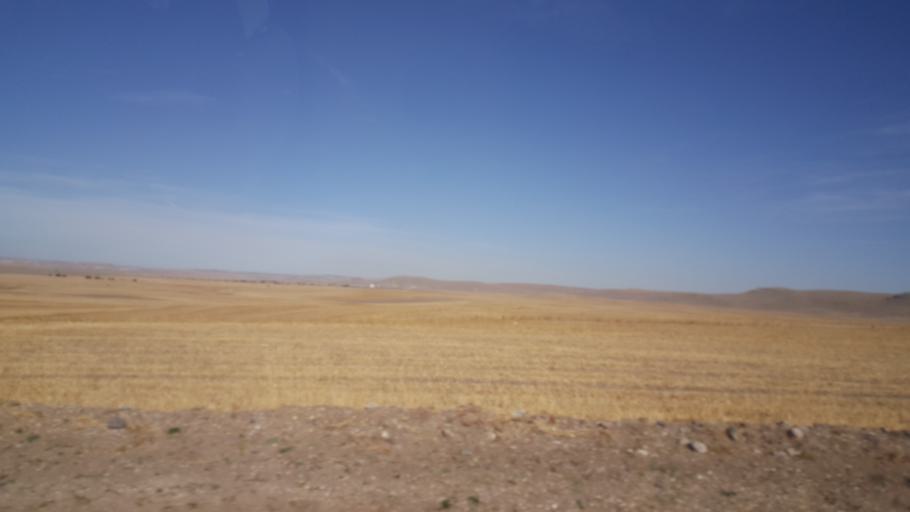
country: TR
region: Ankara
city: Yenice
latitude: 39.3289
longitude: 32.7545
